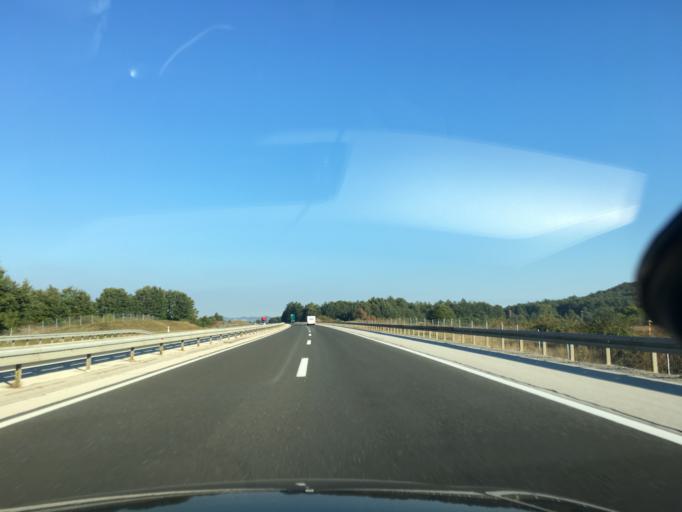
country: HR
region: Zadarska
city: Obrovac
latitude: 44.4258
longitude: 15.6343
